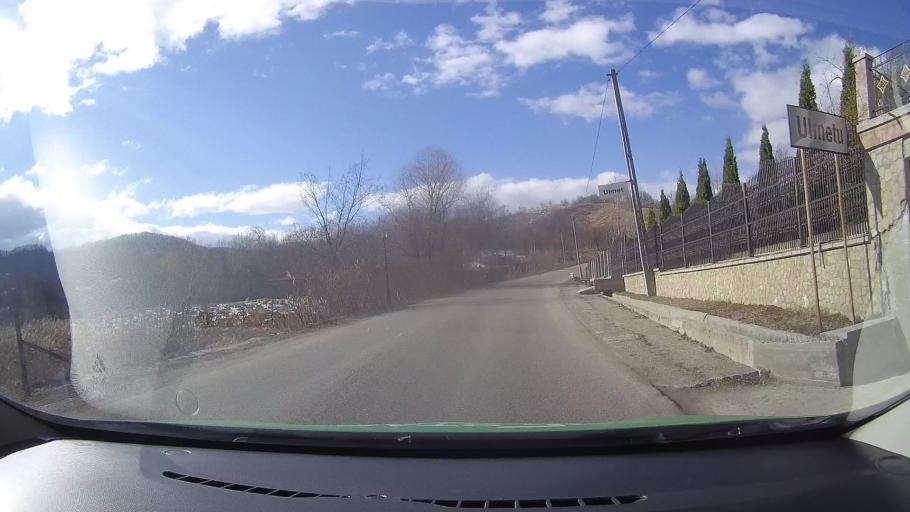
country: RO
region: Dambovita
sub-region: Oras Pucioasa
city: Glodeni
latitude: 45.0910
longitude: 25.4768
